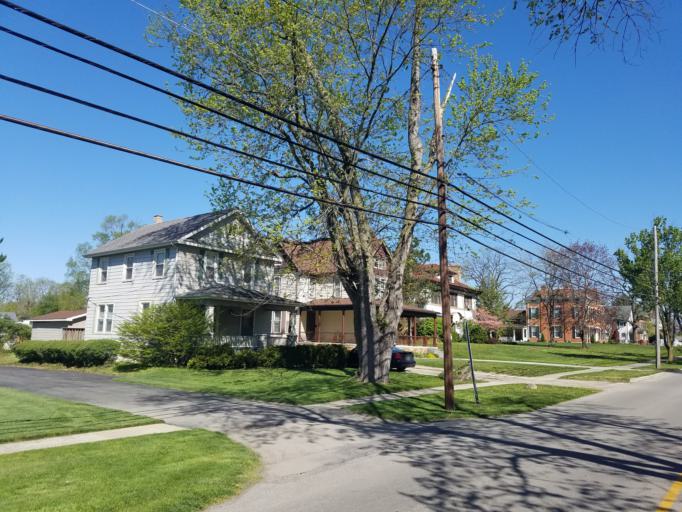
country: US
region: Ohio
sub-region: Seneca County
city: Tiffin
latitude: 41.1037
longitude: -83.1749
